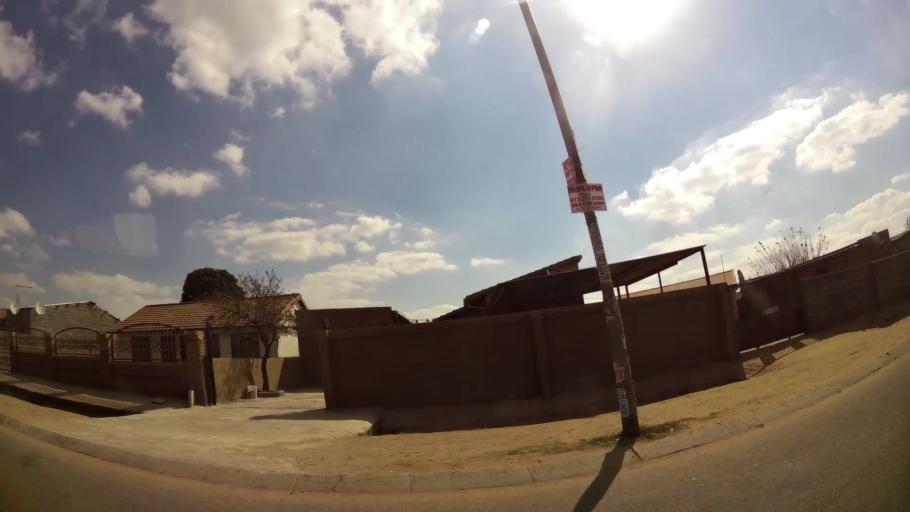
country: ZA
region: Gauteng
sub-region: Ekurhuleni Metropolitan Municipality
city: Tembisa
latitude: -26.0187
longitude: 28.1916
